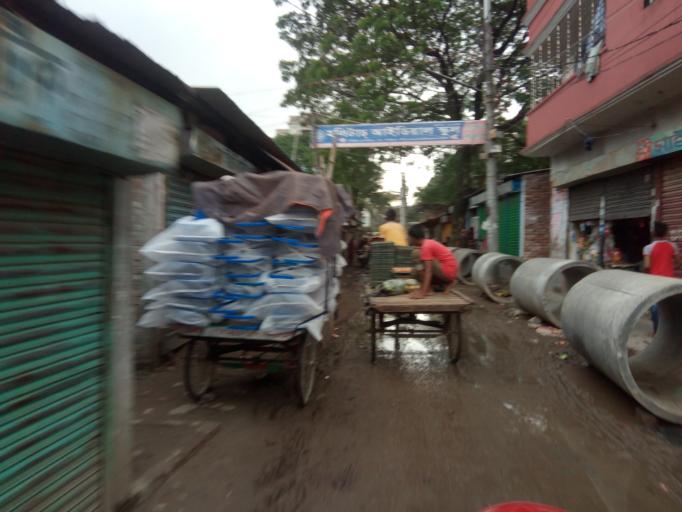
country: BD
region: Dhaka
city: Azimpur
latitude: 23.7185
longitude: 90.3639
